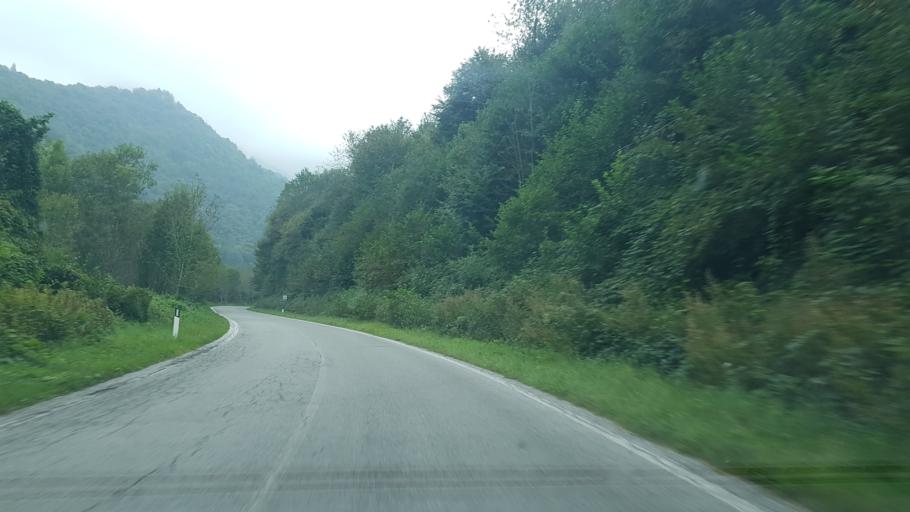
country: IT
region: Piedmont
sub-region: Provincia di Cuneo
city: Roccaforte Mondovi
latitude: 44.2843
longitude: 7.7437
